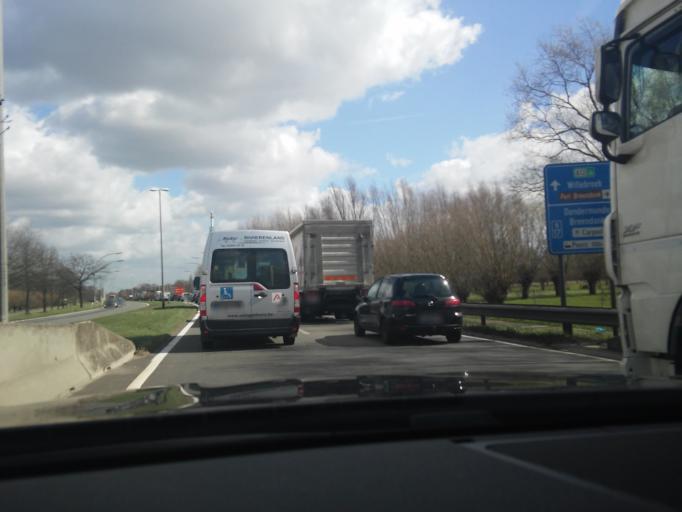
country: BE
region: Flanders
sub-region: Provincie Antwerpen
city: Willebroek
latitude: 51.0612
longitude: 4.3284
